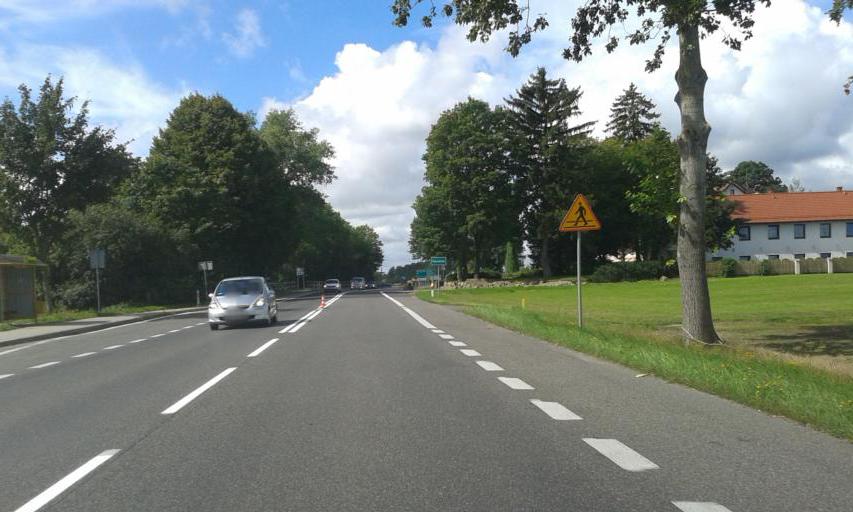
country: PL
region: West Pomeranian Voivodeship
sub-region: Powiat slawienski
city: Slawno
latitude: 54.3281
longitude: 16.5684
